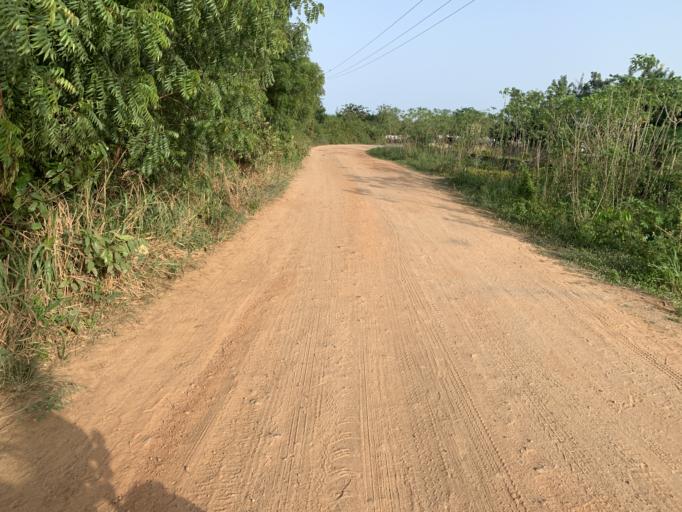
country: GH
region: Central
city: Winneba
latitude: 5.3901
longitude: -0.6020
